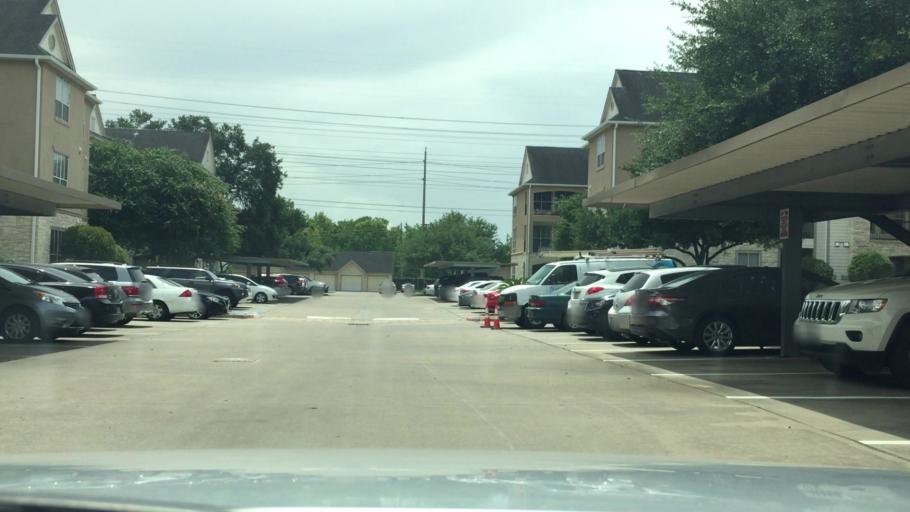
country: US
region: Texas
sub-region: Harris County
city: Bellaire
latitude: 29.7232
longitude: -95.4700
